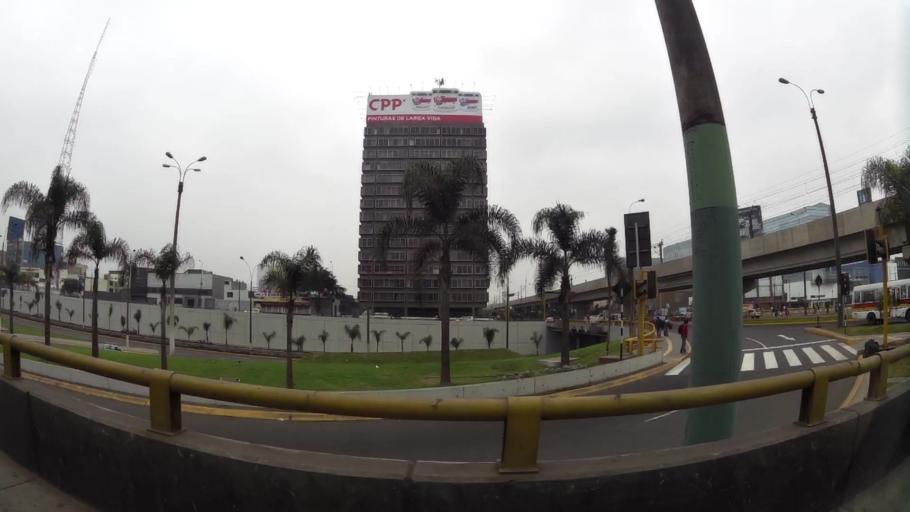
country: PE
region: Lima
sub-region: Lima
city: San Luis
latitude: -12.0874
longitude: -77.0034
